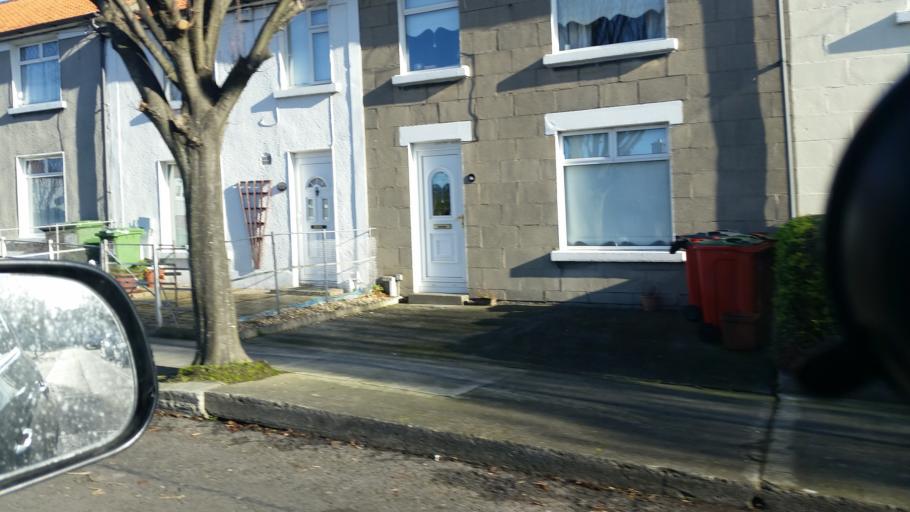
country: IE
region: Leinster
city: Marino
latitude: 53.3653
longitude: -6.2332
